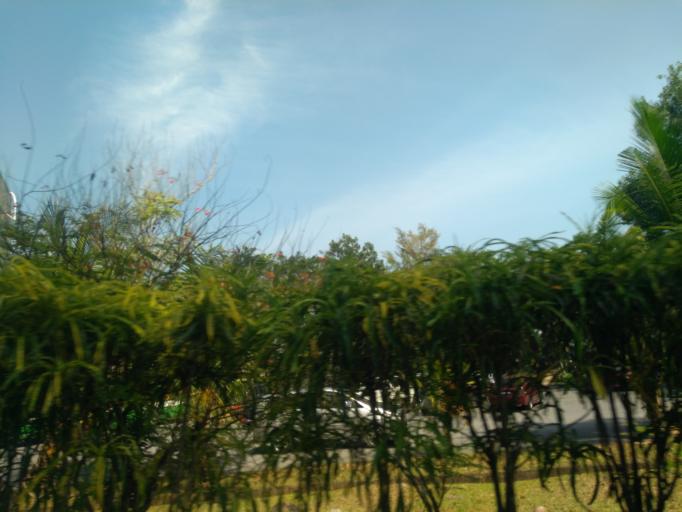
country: MY
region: Sarawak
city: Kuching
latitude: 1.7499
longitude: 110.3155
